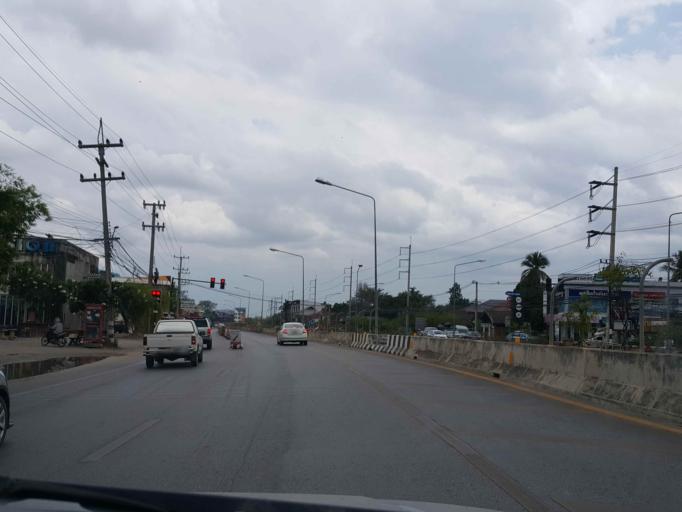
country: TH
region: Chiang Mai
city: Chiang Mai
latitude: 18.7843
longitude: 98.9585
